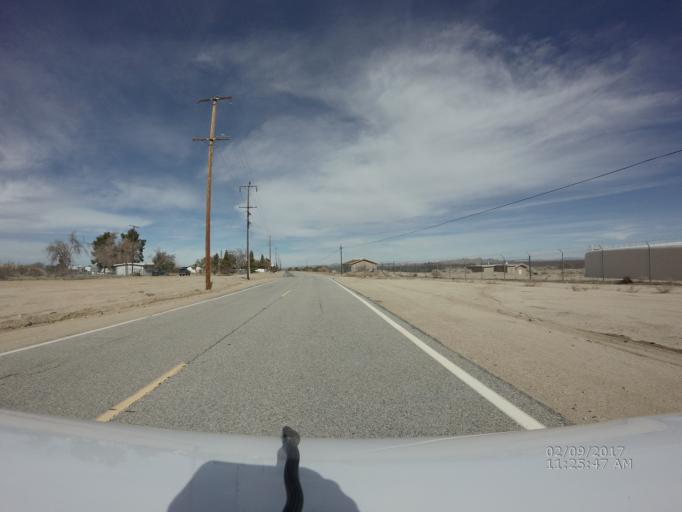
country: US
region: California
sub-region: Los Angeles County
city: Littlerock
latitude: 34.5241
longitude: -117.9230
